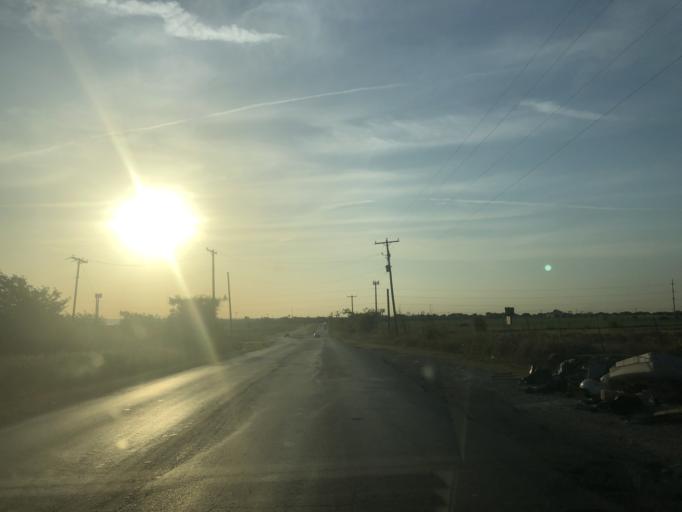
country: US
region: Texas
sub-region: Tarrant County
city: White Settlement
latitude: 32.7744
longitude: -97.4839
